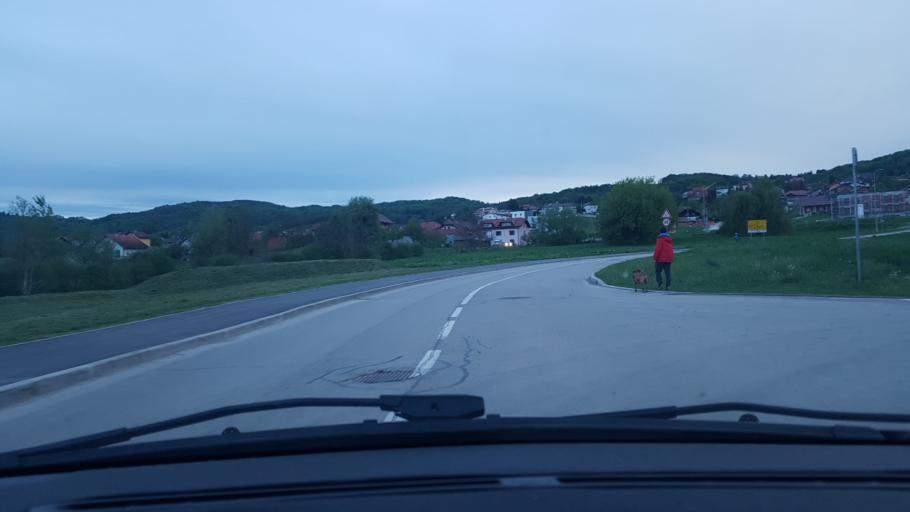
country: HR
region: Zagrebacka
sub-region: Grad Samobor
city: Samobor
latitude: 45.7930
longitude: 15.7223
